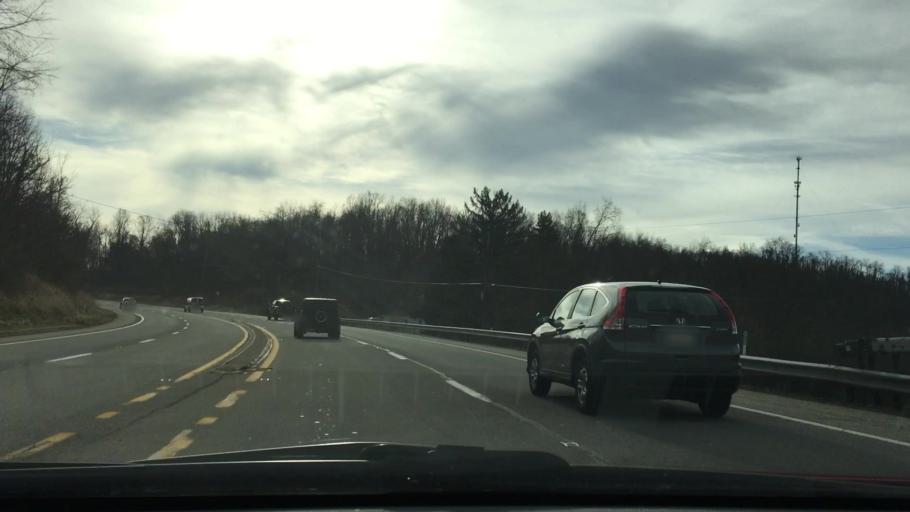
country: US
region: Pennsylvania
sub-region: Fayette County
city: Perryopolis
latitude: 40.0259
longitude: -79.7714
